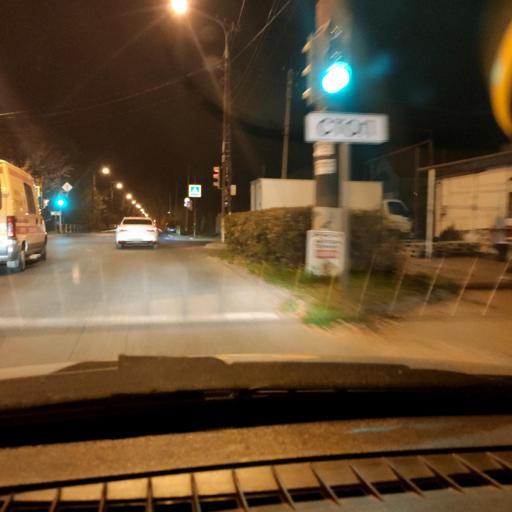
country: RU
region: Samara
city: Tol'yatti
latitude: 53.5098
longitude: 49.3950
